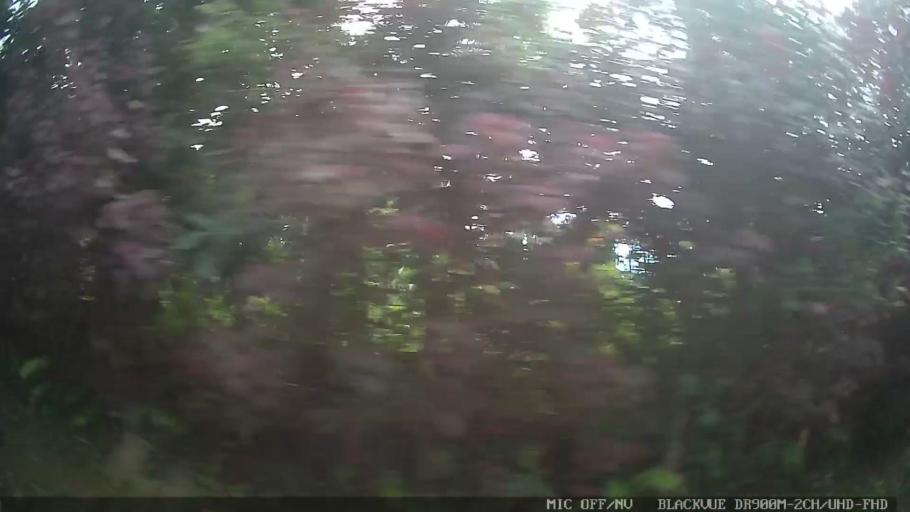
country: BR
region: Sao Paulo
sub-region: Rio Grande Da Serra
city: Rio Grande da Serra
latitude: -23.6904
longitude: -46.3176
